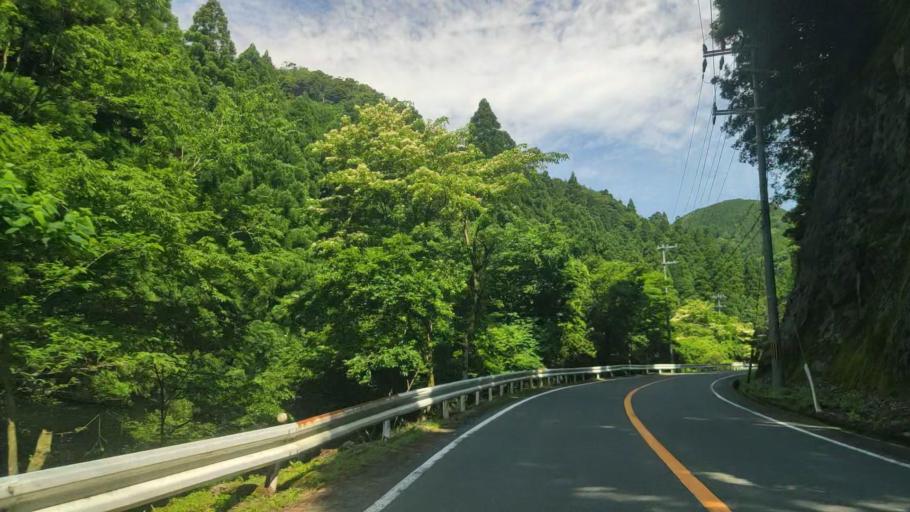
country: JP
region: Hyogo
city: Toyooka
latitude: 35.6325
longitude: 134.7809
